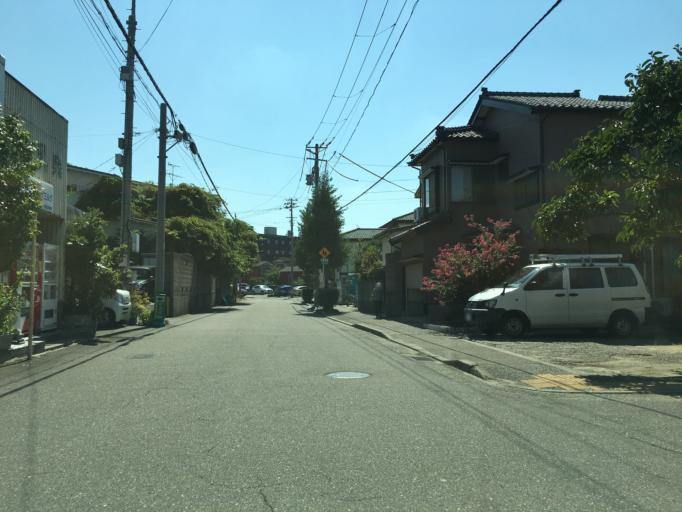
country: JP
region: Niigata
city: Niigata-shi
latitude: 37.9096
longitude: 139.0164
